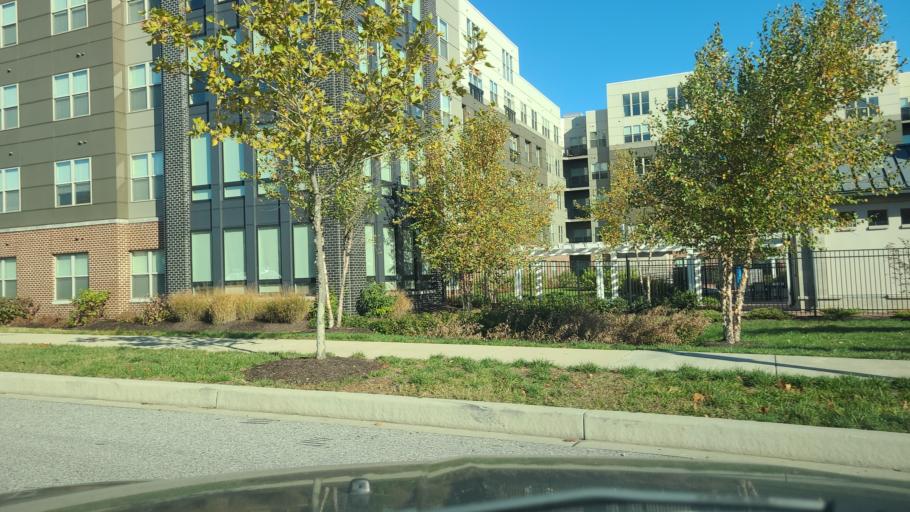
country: US
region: Maryland
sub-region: Howard County
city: Fort George G Mead Junction
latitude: 39.1245
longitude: -76.7961
